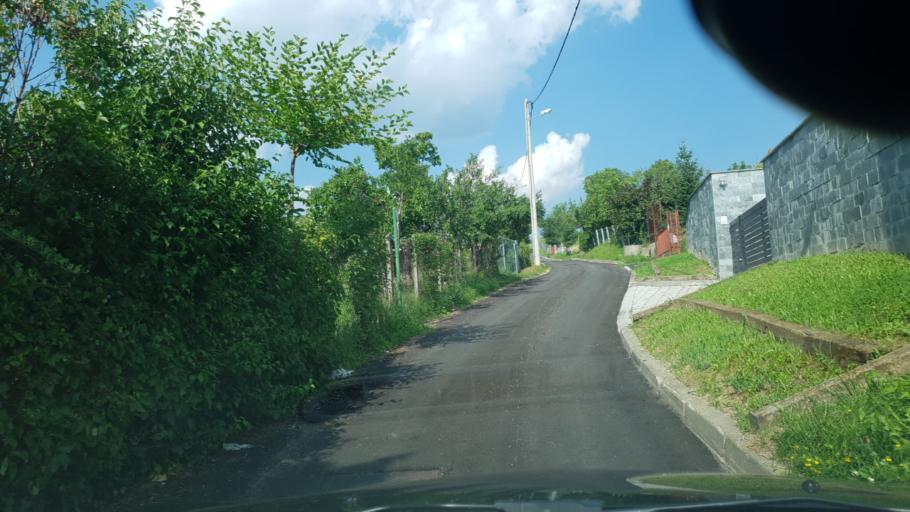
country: HR
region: Grad Zagreb
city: Stenjevec
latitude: 45.8375
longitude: 15.9074
